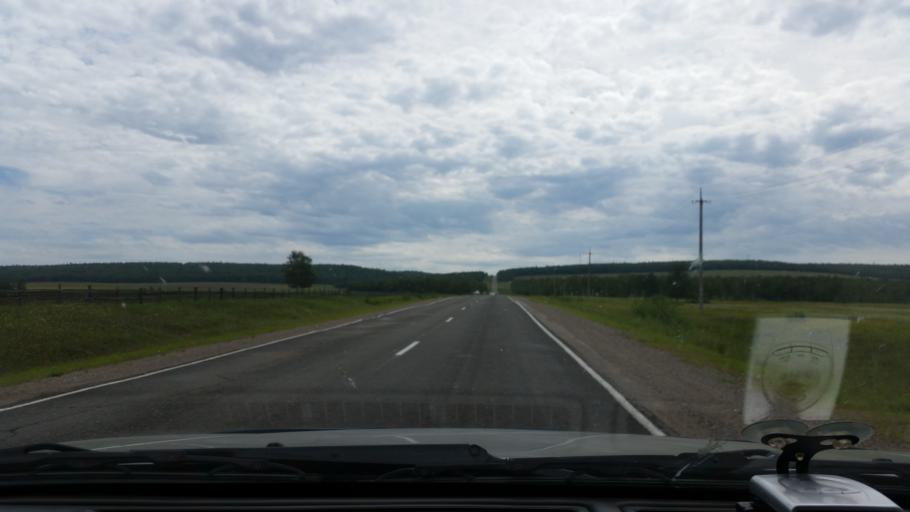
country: RU
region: Irkutsk
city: Bayanday
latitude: 53.0468
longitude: 105.5449
